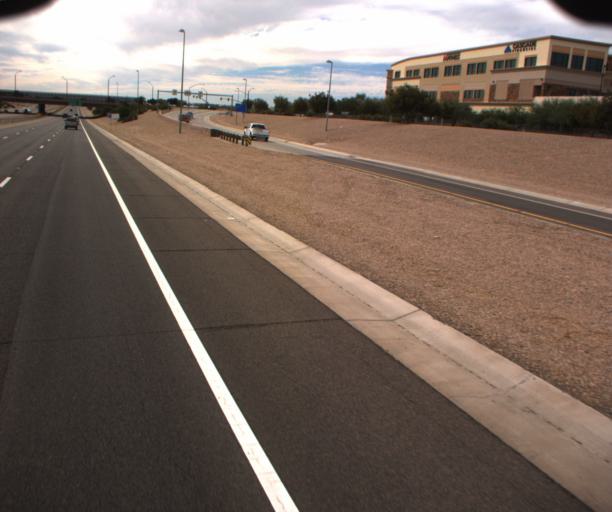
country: US
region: Arizona
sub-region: Maricopa County
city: Gilbert
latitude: 33.2902
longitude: -111.7526
